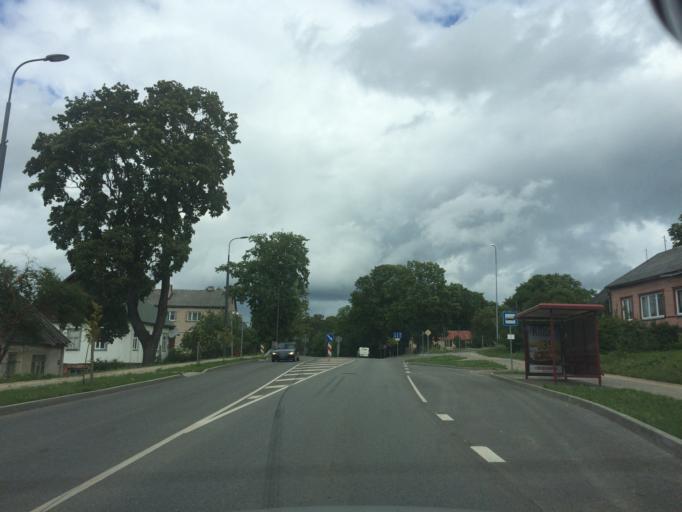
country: LV
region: Rezekne
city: Rezekne
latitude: 56.4954
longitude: 27.3212
